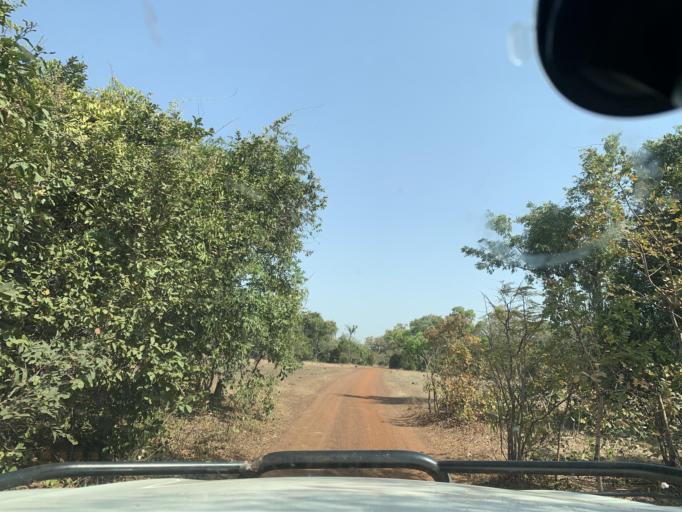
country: ML
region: Sikasso
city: Kolondieba
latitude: 10.8964
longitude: -6.7438
